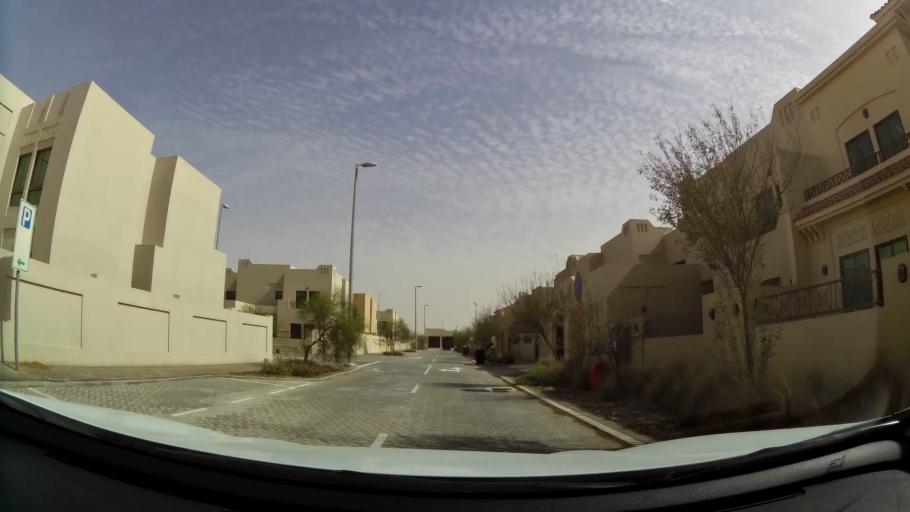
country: AE
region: Abu Dhabi
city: Abu Dhabi
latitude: 24.4055
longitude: 54.5345
